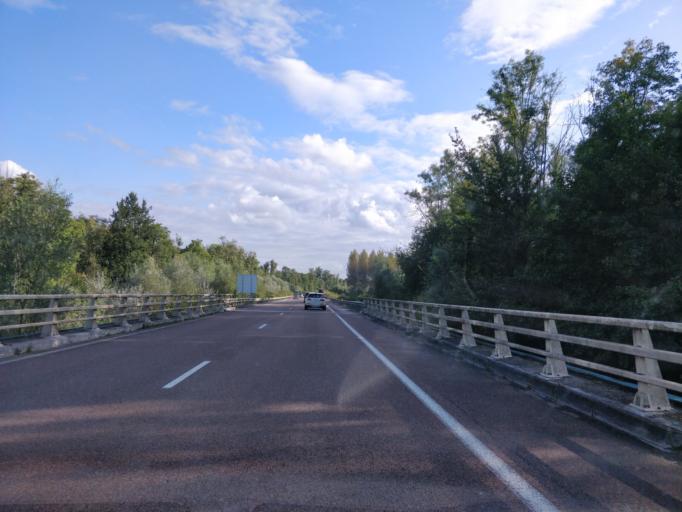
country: FR
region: Champagne-Ardenne
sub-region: Departement de l'Aube
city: Saint-Julien-les-Villas
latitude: 48.2596
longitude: 4.1160
